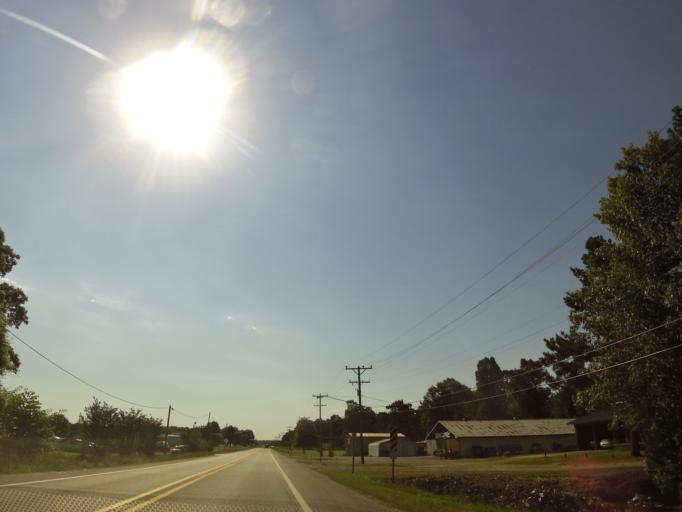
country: US
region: Arkansas
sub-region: Clay County
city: Corning
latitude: 36.4070
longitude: -90.5777
